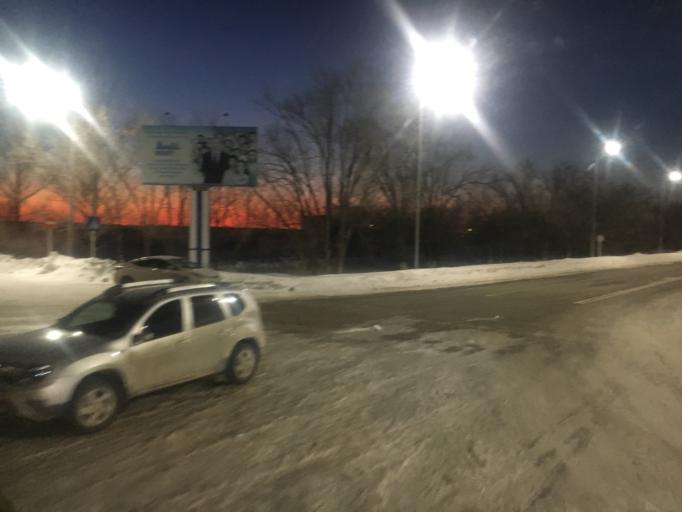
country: KZ
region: Batys Qazaqstan
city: Oral
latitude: 51.1540
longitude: 51.5381
